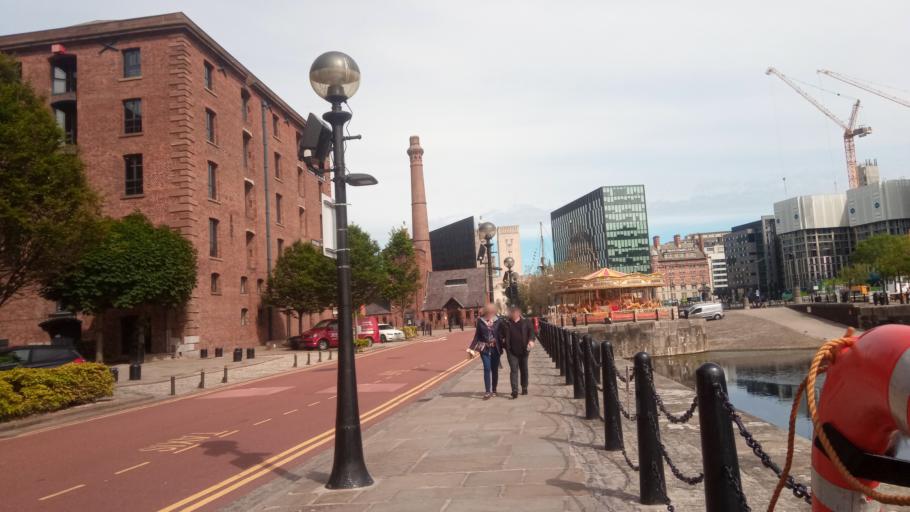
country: GB
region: England
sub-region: Liverpool
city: Liverpool
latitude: 53.4009
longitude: -2.9910
